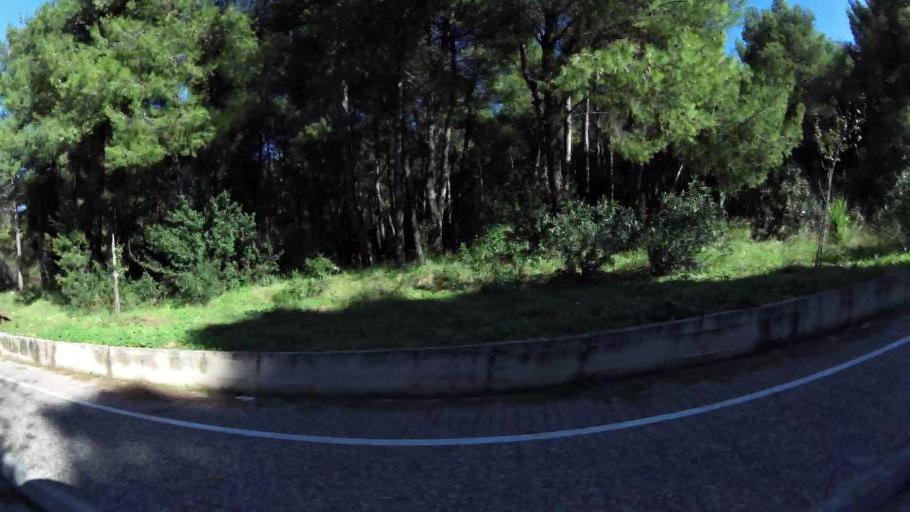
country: GR
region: Attica
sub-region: Nomarchia Anatolikis Attikis
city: Drosia
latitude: 38.1105
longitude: 23.8681
